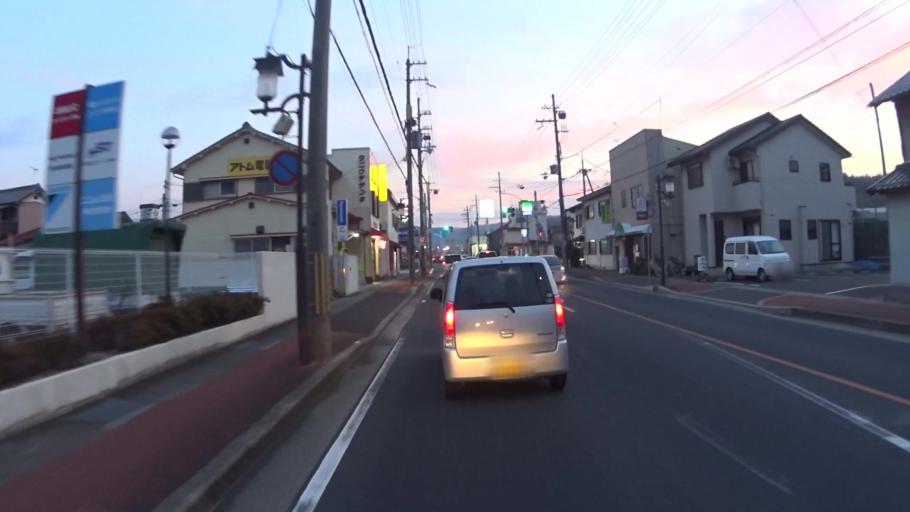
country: JP
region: Kyoto
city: Maizuru
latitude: 35.4376
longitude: 135.3285
